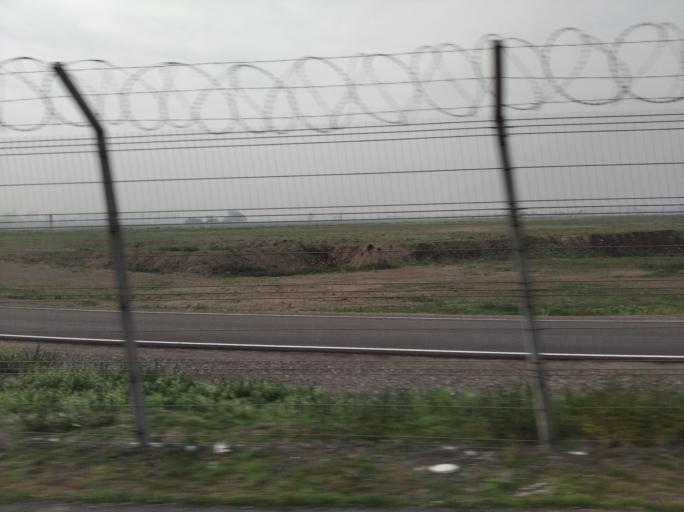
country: CL
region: Santiago Metropolitan
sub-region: Provincia de Chacabuco
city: Lampa
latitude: -33.3681
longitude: -70.8053
